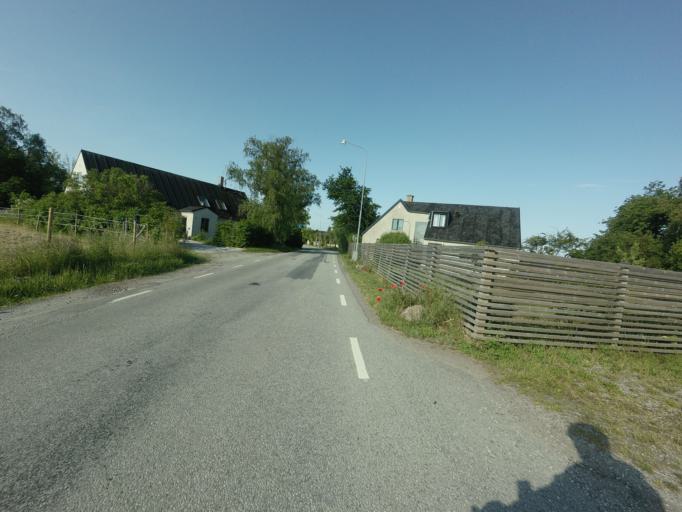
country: SE
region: Skane
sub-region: Trelleborgs Kommun
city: Skare
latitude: 55.4151
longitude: 13.0112
